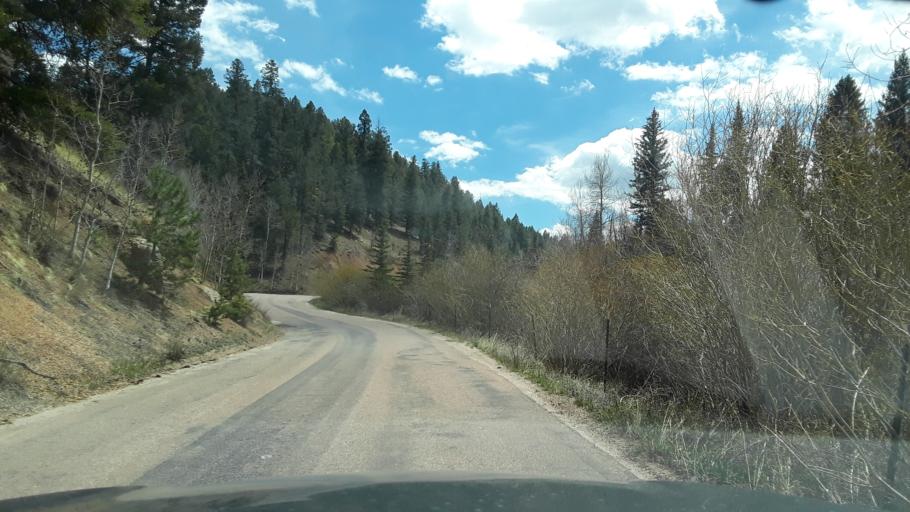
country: US
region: Colorado
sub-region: Teller County
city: Woodland Park
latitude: 39.0158
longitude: -105.0243
